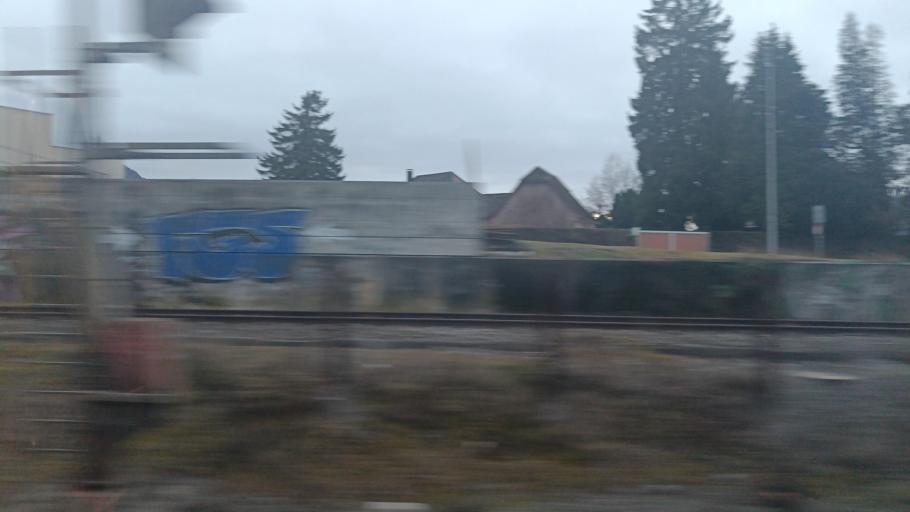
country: CH
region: Aargau
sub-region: Bezirk Laufenburg
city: Frick
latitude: 47.5096
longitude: 8.0146
